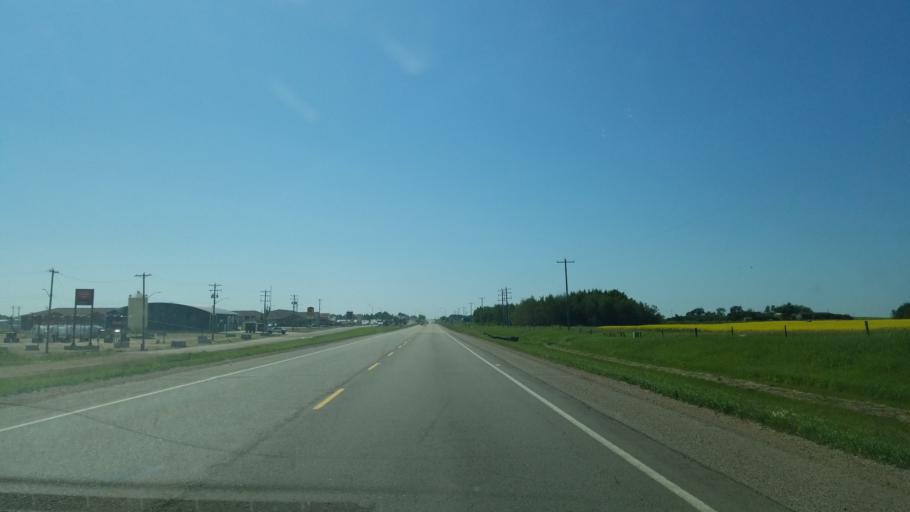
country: CA
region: Alberta
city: Provost
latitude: 52.3612
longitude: -110.2353
